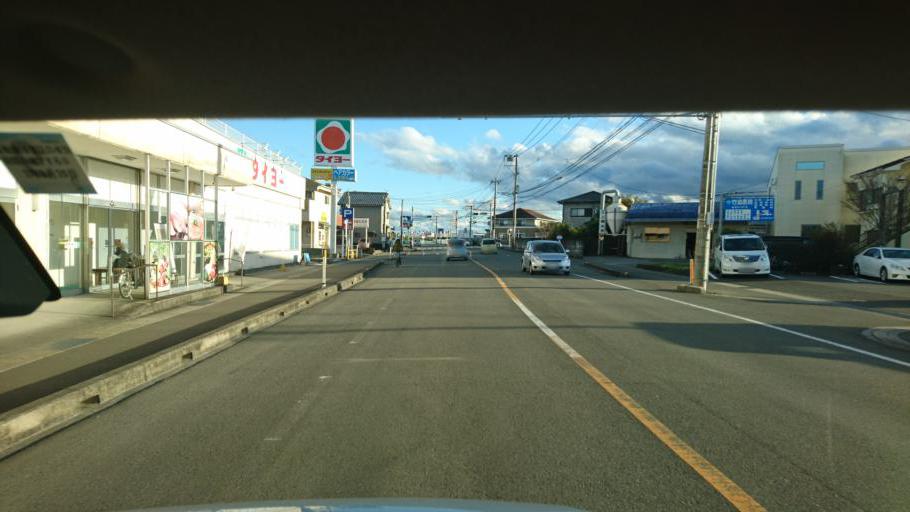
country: JP
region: Miyazaki
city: Miyazaki-shi
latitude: 31.8788
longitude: 131.4284
